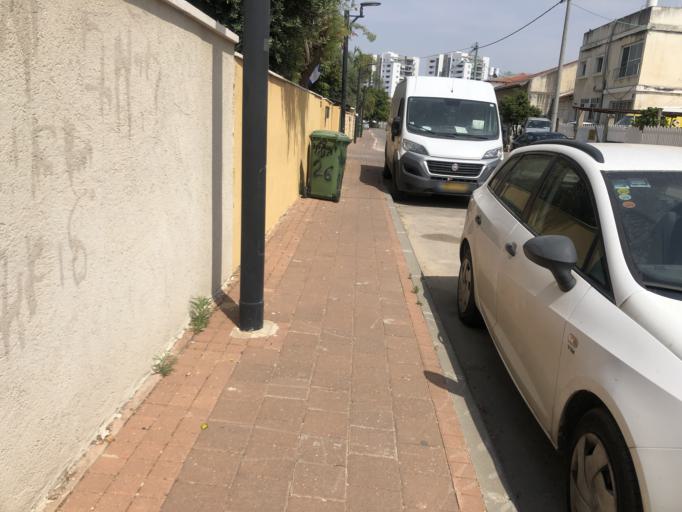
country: IL
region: Central District
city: Rosh Ha'Ayin
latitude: 32.0959
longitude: 34.9405
